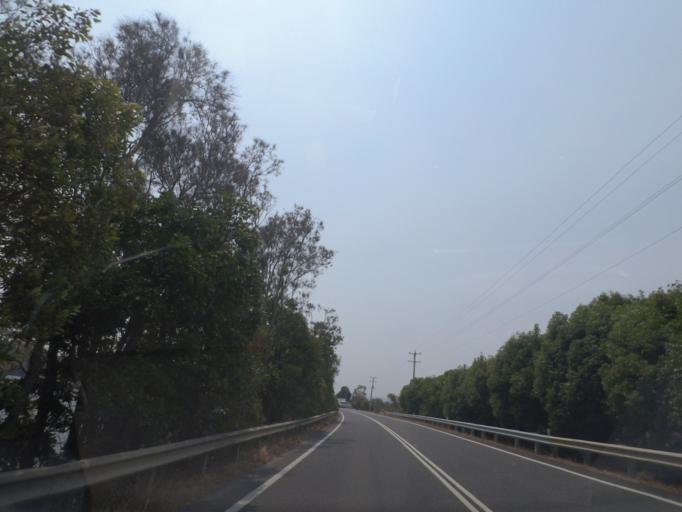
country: AU
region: New South Wales
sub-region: Richmond Valley
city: Evans Head
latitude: -28.9790
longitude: 153.4622
